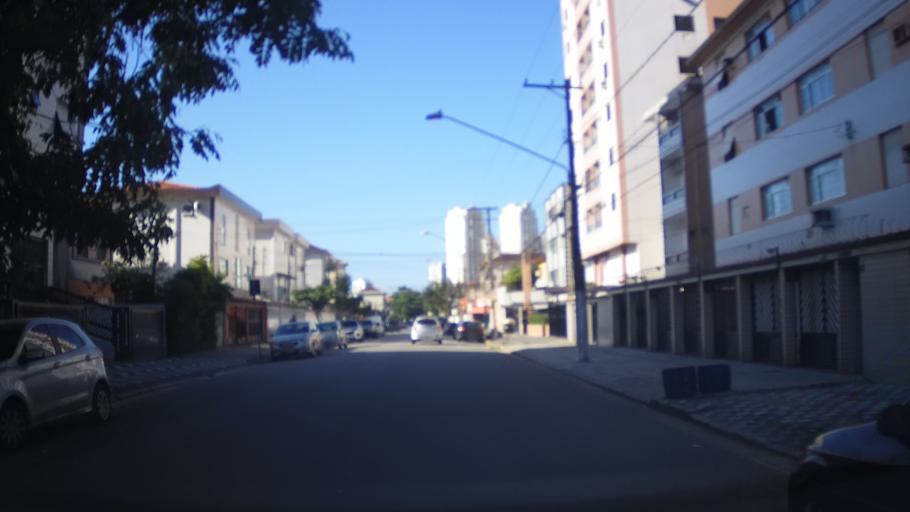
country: BR
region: Sao Paulo
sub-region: Santos
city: Santos
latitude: -23.9526
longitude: -46.3477
